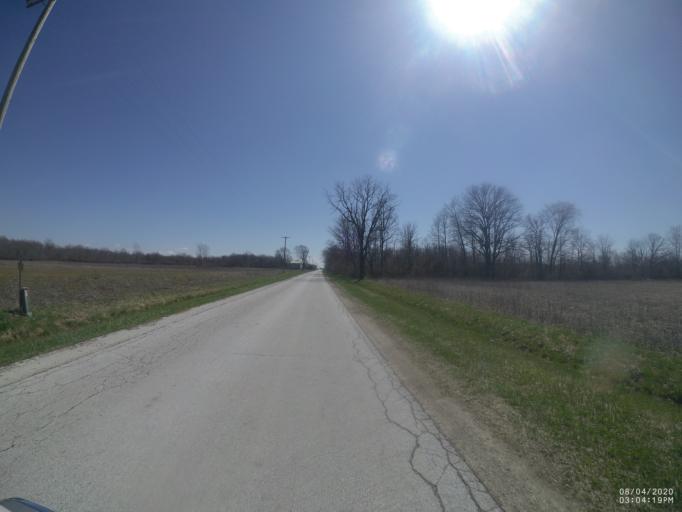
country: US
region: Ohio
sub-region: Sandusky County
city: Stony Prairie
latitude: 41.3191
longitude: -83.2401
